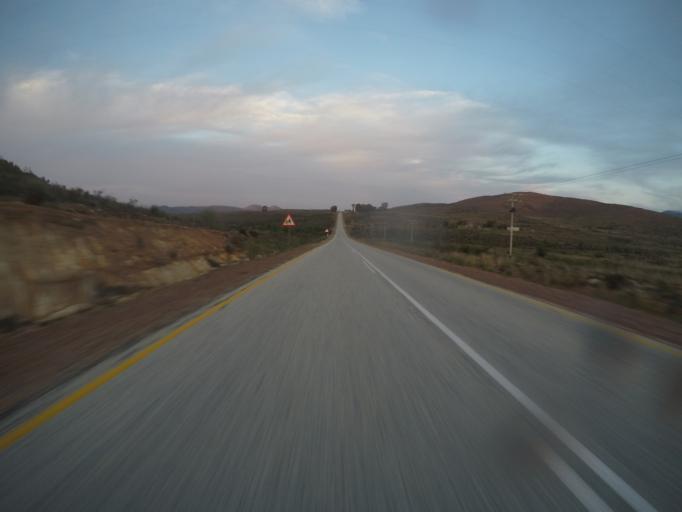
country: ZA
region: Western Cape
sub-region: Eden District Municipality
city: Plettenberg Bay
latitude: -33.7393
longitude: 23.4283
